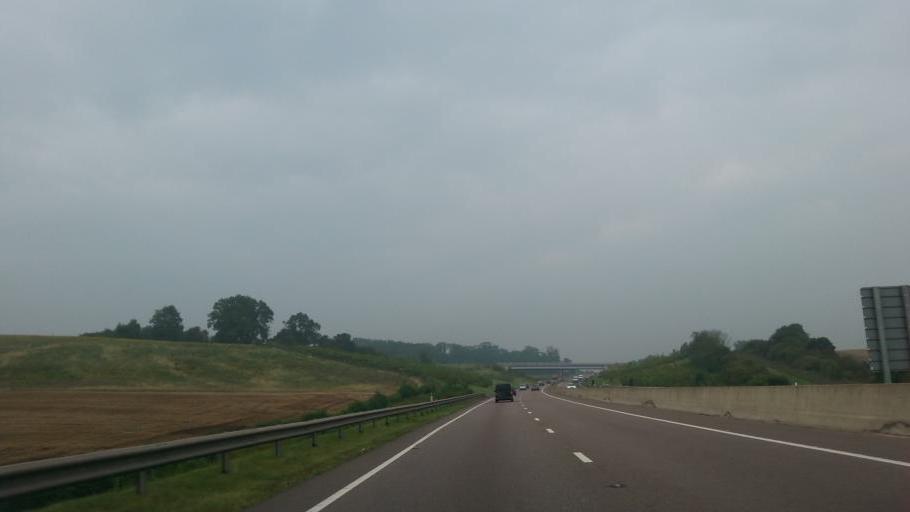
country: GB
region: England
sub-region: Nottinghamshire
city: Cotgrave
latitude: 52.9128
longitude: -1.0131
